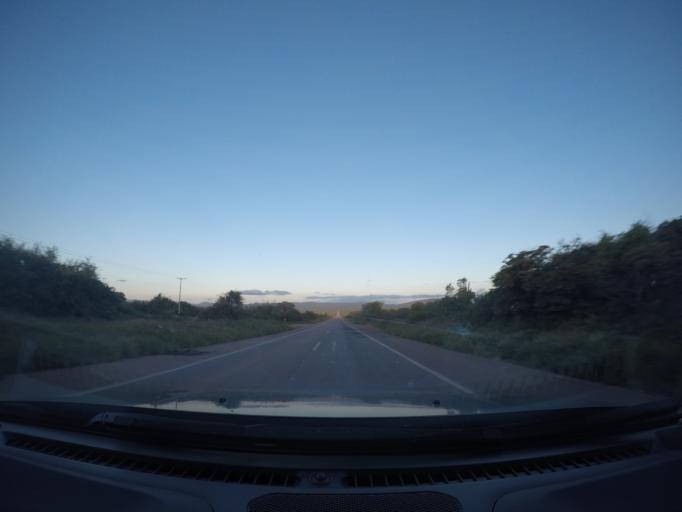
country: BR
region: Bahia
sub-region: Seabra
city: Seabra
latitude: -12.4098
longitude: -41.9678
